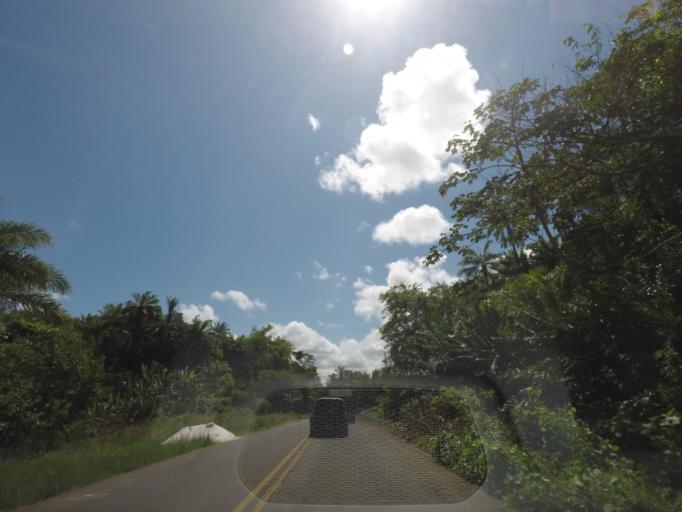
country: BR
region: Bahia
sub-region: Valenca
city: Valenca
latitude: -13.4461
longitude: -39.0837
